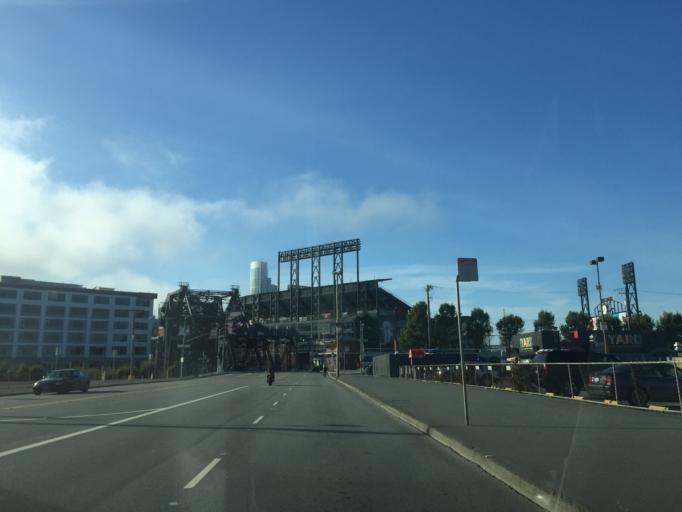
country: US
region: California
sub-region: San Francisco County
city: San Francisco
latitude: 37.7753
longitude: -122.3899
